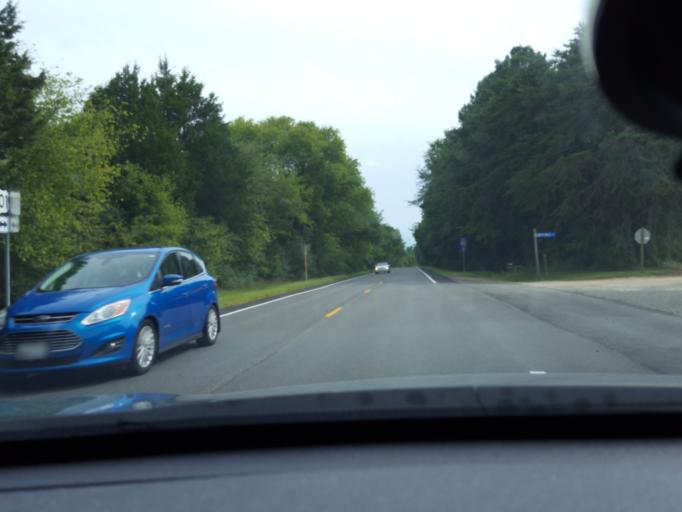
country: US
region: Virginia
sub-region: Hanover County
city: Hanover
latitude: 37.7972
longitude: -77.3712
